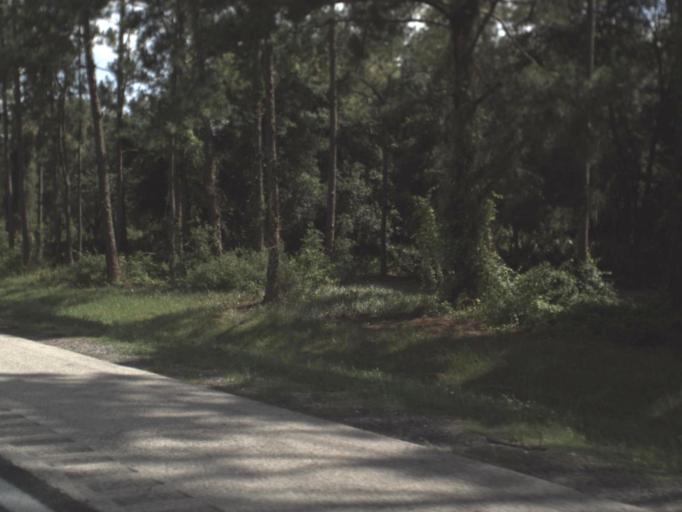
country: US
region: Florida
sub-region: Alachua County
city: Gainesville
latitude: 29.5038
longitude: -82.2977
